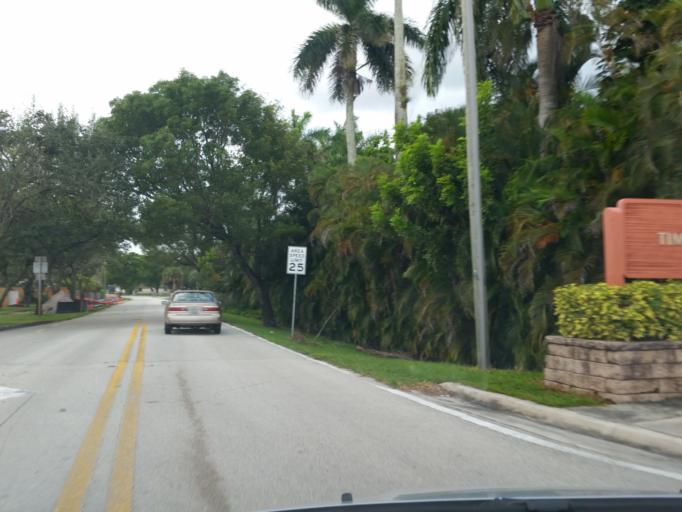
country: US
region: Florida
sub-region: Broward County
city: Cooper City
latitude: 26.0643
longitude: -80.2631
